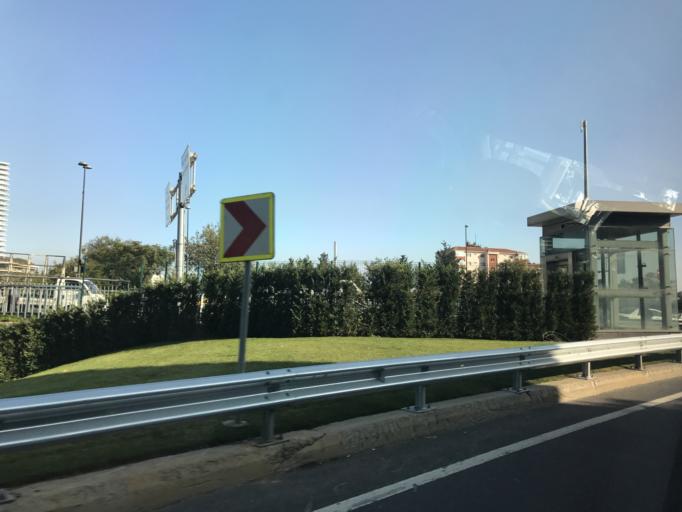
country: TR
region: Istanbul
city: Sisli
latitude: 41.0653
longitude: 29.0118
